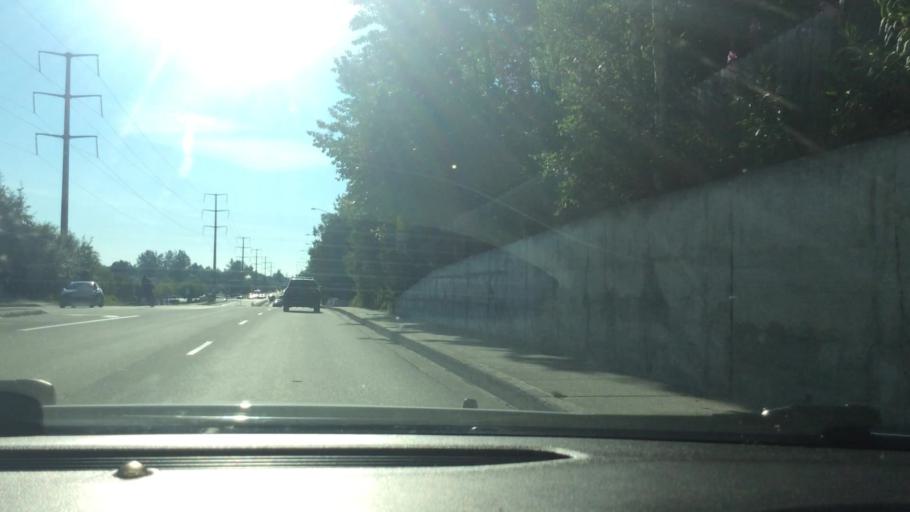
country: US
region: Alaska
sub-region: Anchorage Municipality
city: Anchorage
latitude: 61.1953
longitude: -149.7724
